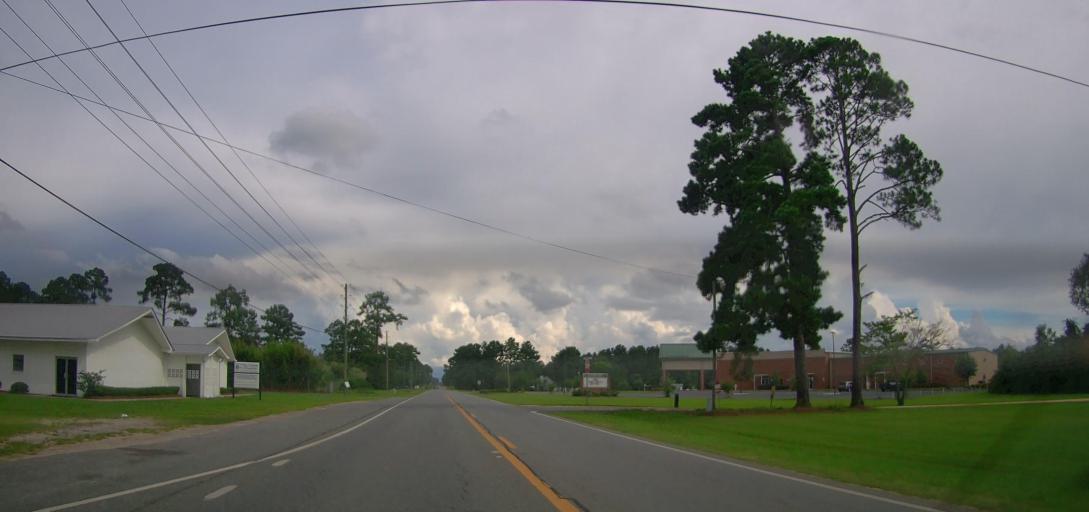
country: US
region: Georgia
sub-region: Wayne County
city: Jesup
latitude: 31.6572
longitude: -81.9129
